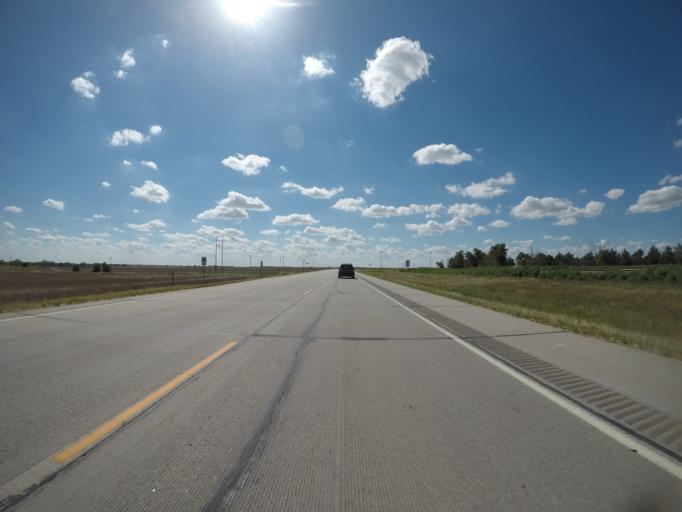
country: US
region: Colorado
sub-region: Phillips County
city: Holyoke
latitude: 40.5933
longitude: -102.3580
